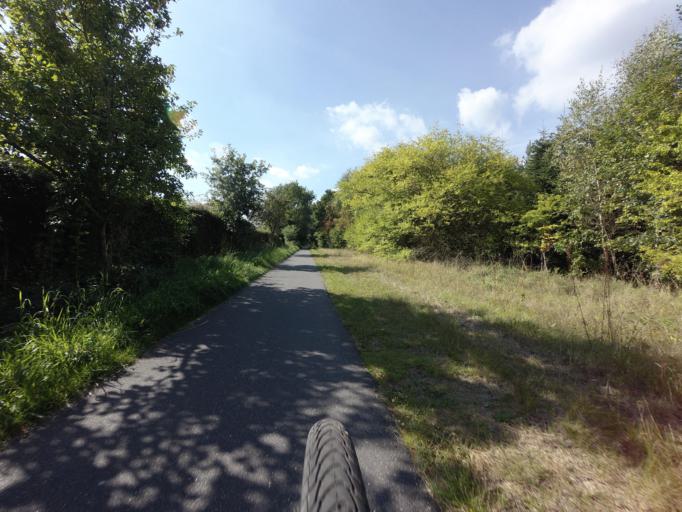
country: DK
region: Central Jutland
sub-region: Viborg Kommune
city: Viborg
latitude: 56.4182
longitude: 9.3745
